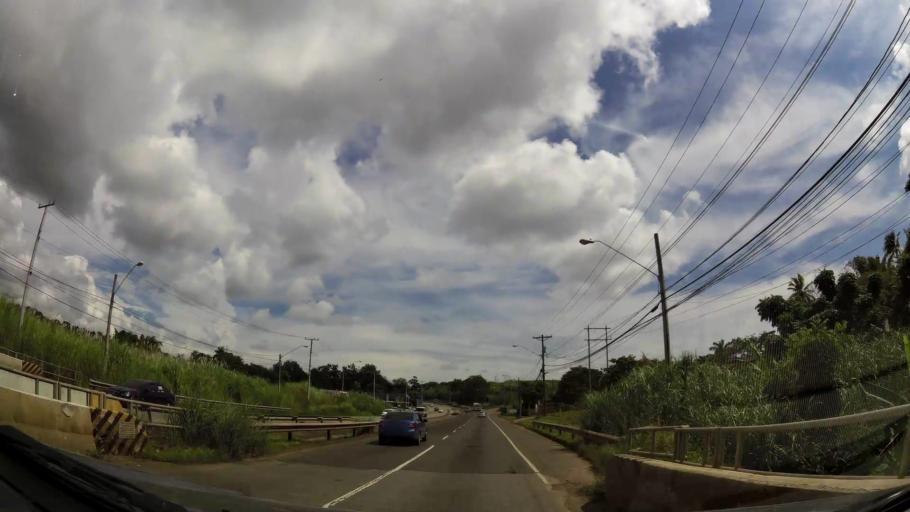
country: PA
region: Panama
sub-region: Distrito Arraijan
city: Arraijan
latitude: 8.9507
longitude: -79.6668
